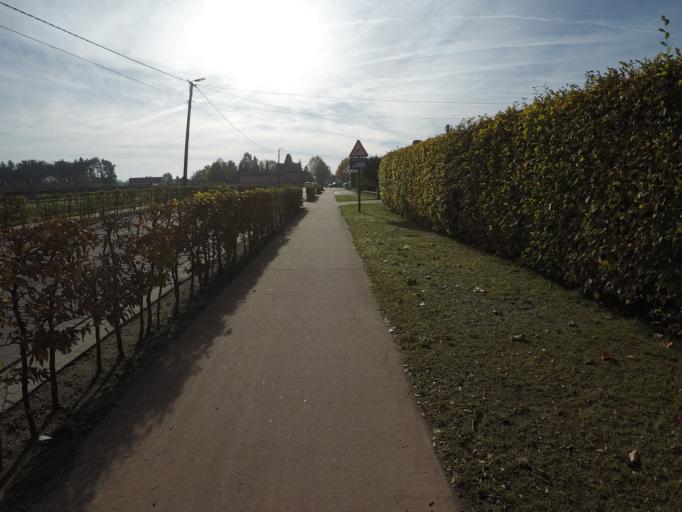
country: BE
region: Flanders
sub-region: Provincie Vlaams-Brabant
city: Begijnendijk
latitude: 50.9992
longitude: 4.7890
